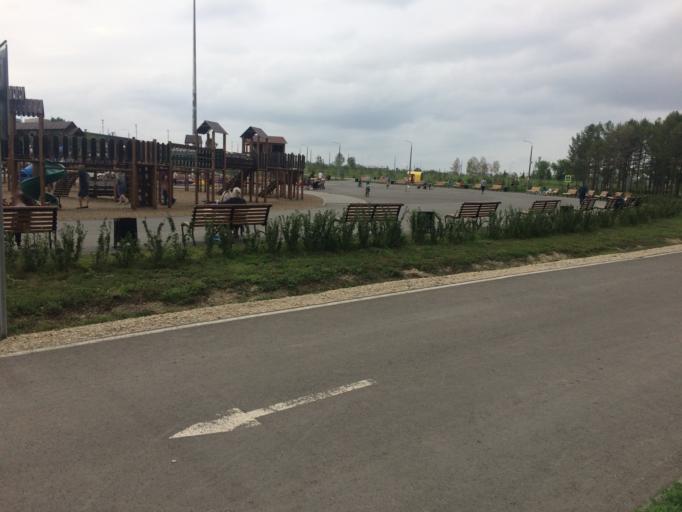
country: RU
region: Chelyabinsk
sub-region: Gorod Magnitogorsk
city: Magnitogorsk
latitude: 53.4038
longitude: 58.9896
